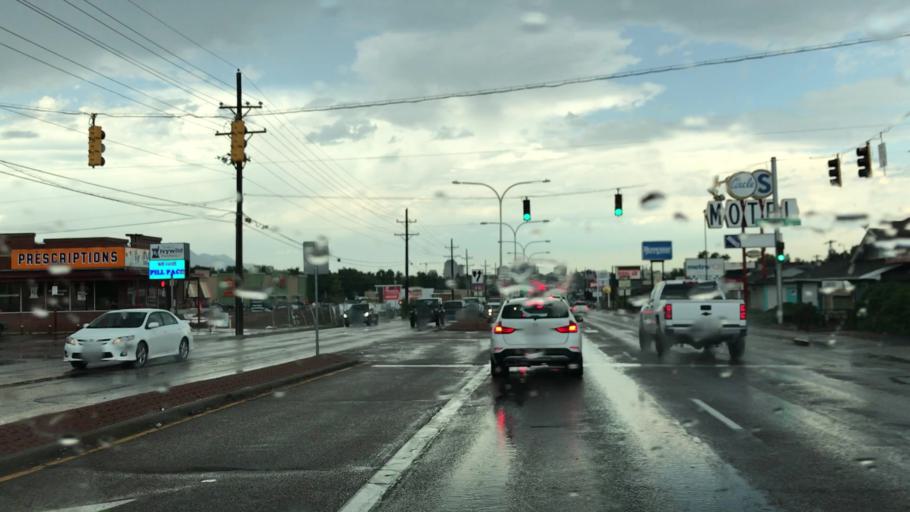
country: US
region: Colorado
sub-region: El Paso County
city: Colorado Springs
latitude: 38.8094
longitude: -104.8223
